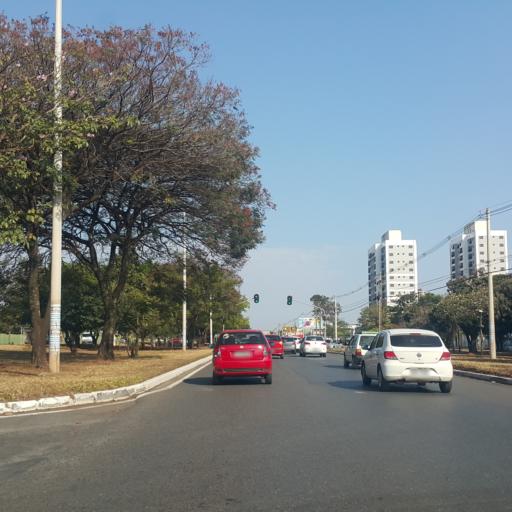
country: BR
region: Federal District
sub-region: Brasilia
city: Brasilia
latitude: -15.8625
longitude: -48.0351
